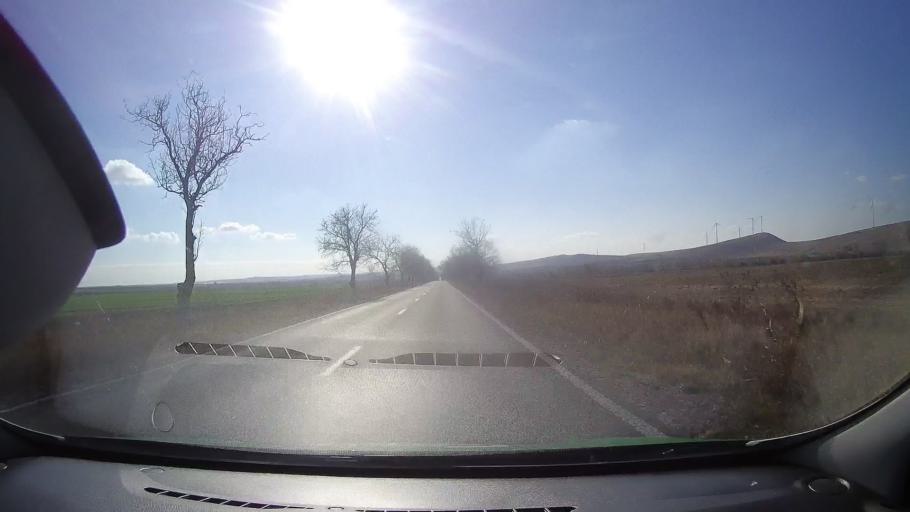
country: RO
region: Tulcea
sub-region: Comuna Ceamurlia de Jos
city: Ceamurlia de Jos
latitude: 44.7859
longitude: 28.6895
